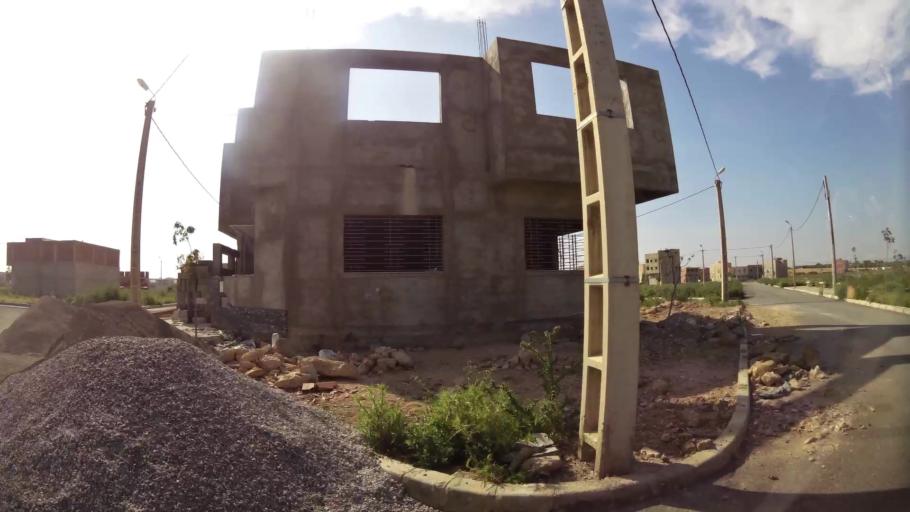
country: MA
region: Oriental
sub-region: Oujda-Angad
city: Oujda
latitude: 34.7086
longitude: -1.8780
